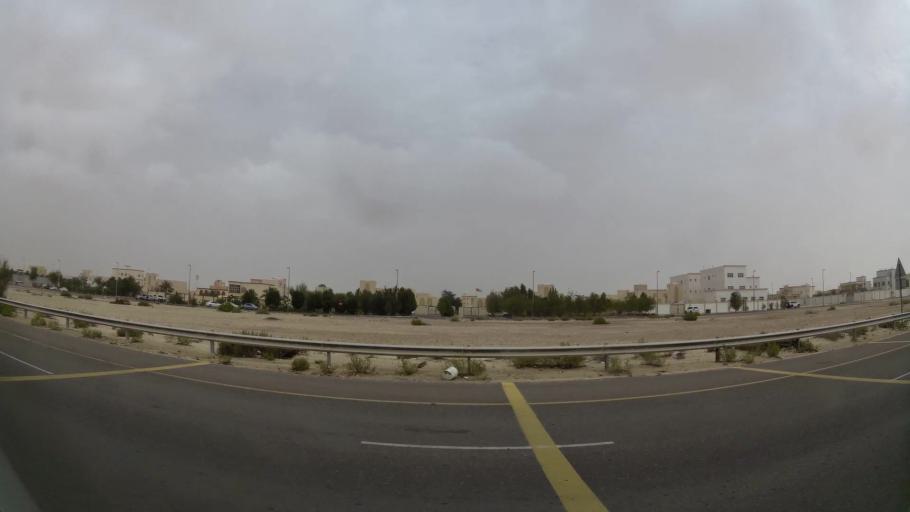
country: AE
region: Abu Dhabi
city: Abu Dhabi
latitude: 24.3828
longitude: 54.7248
